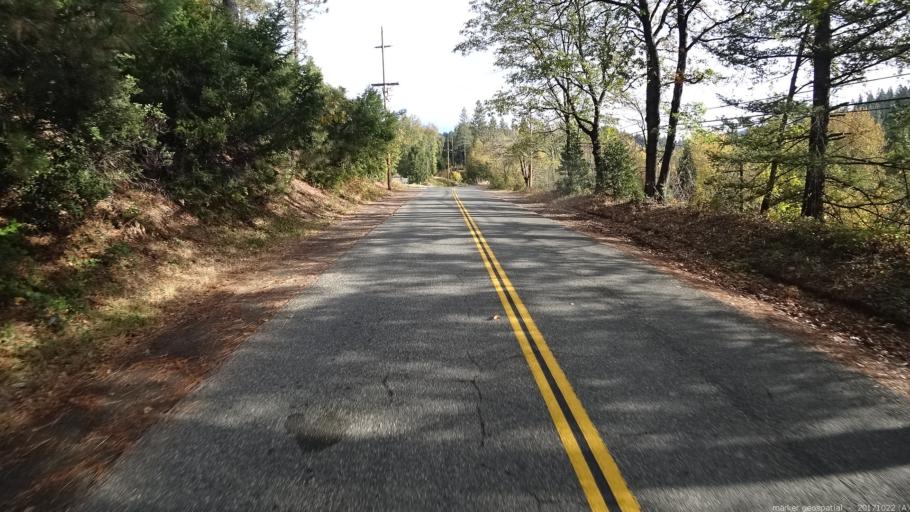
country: US
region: California
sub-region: Siskiyou County
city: Dunsmuir
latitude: 41.1473
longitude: -122.3159
